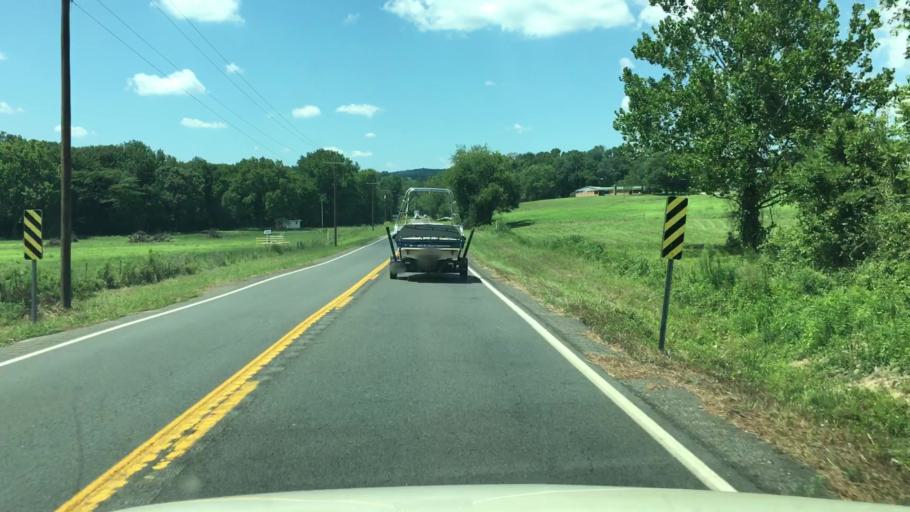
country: US
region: Arkansas
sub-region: Garland County
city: Lake Hamilton
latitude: 34.3340
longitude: -93.1774
